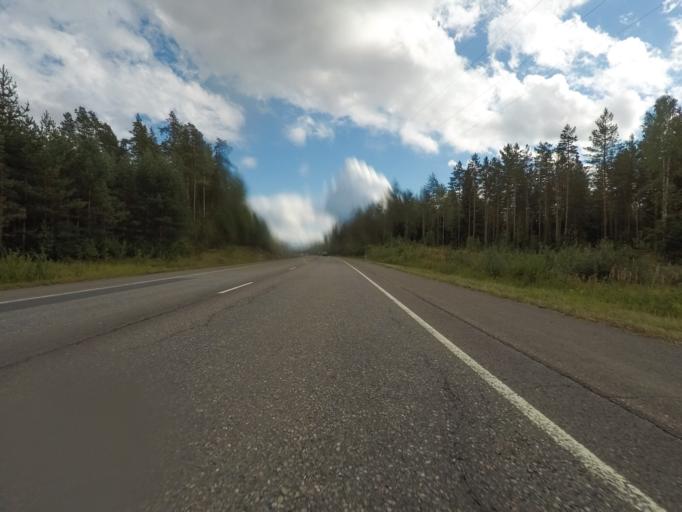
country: FI
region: Paijanne Tavastia
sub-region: Lahti
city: Heinola
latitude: 61.3080
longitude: 26.0477
